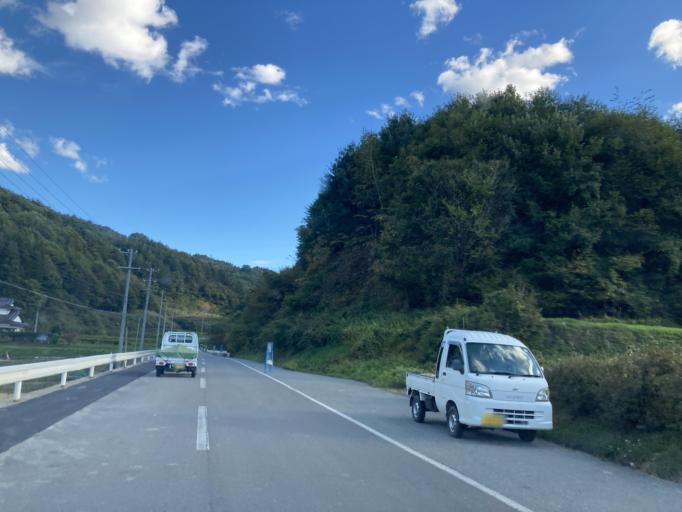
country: JP
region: Nagano
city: Ueda
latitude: 36.4155
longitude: 138.1045
